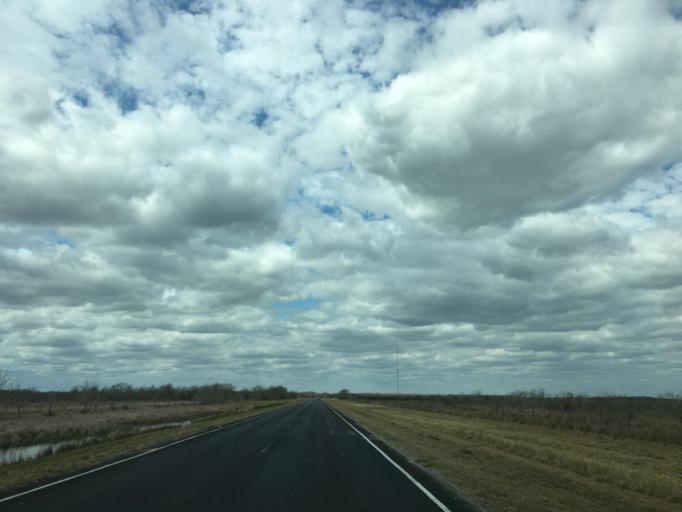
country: US
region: Texas
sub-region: Brazoria County
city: Oyster Creek
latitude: 29.0655
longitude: -95.3025
